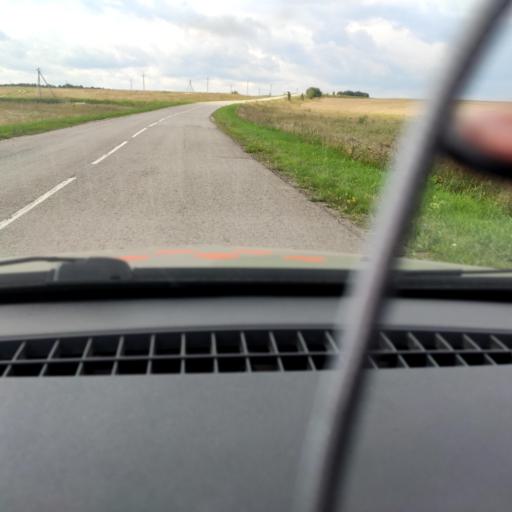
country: RU
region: Bashkortostan
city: Iglino
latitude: 54.7637
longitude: 56.5569
